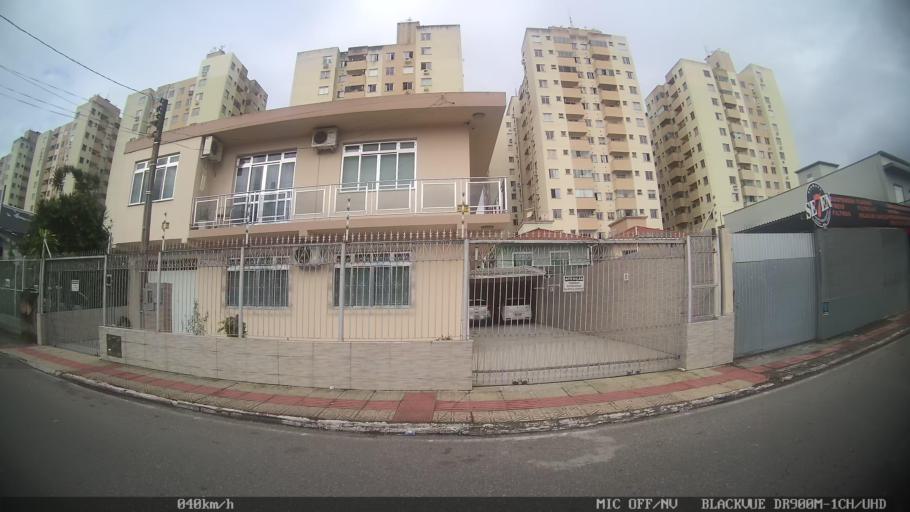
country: BR
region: Santa Catarina
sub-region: Sao Jose
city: Campinas
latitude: -27.5572
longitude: -48.6256
